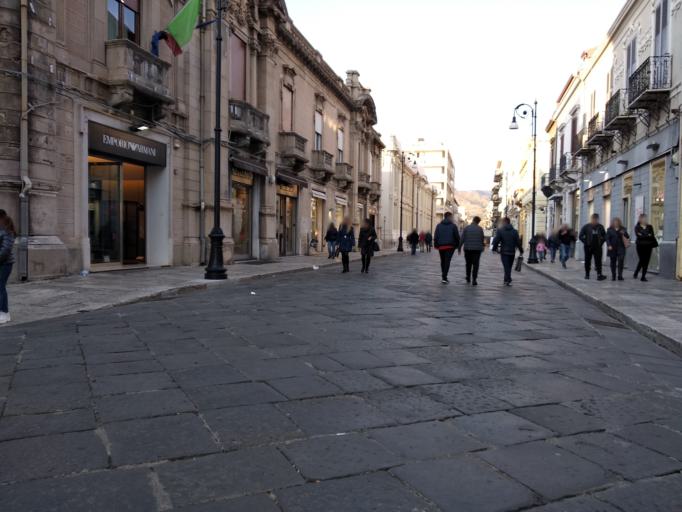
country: IT
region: Calabria
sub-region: Provincia di Reggio Calabria
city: Reggio Calabria
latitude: 38.1106
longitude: 15.6466
